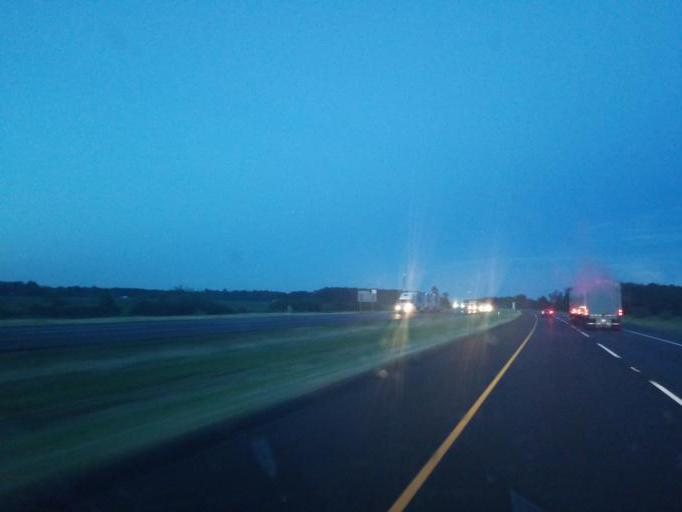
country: US
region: Indiana
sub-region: Saint Joseph County
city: Granger
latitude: 41.7318
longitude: -86.0959
